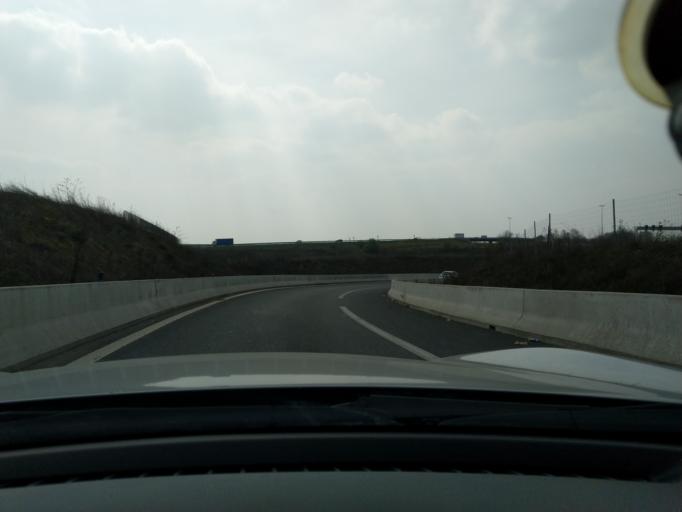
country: FR
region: Ile-de-France
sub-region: Departement du Val-d'Oise
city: Roissy-en-France
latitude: 49.0294
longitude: 2.5408
